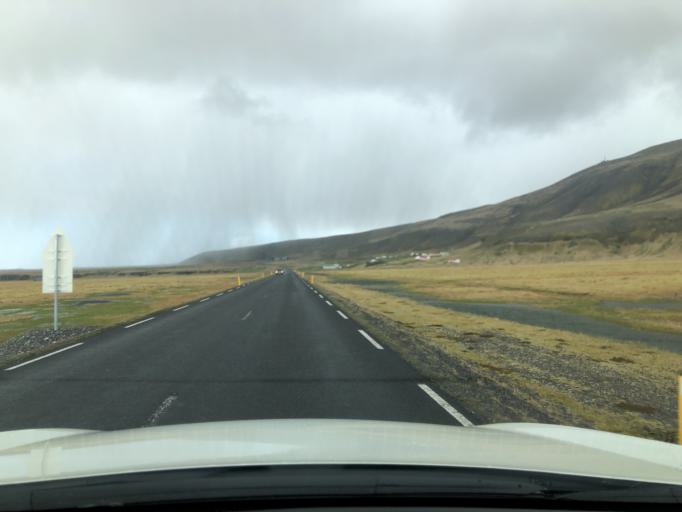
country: IS
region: East
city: Hoefn
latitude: 63.9081
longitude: -16.5658
